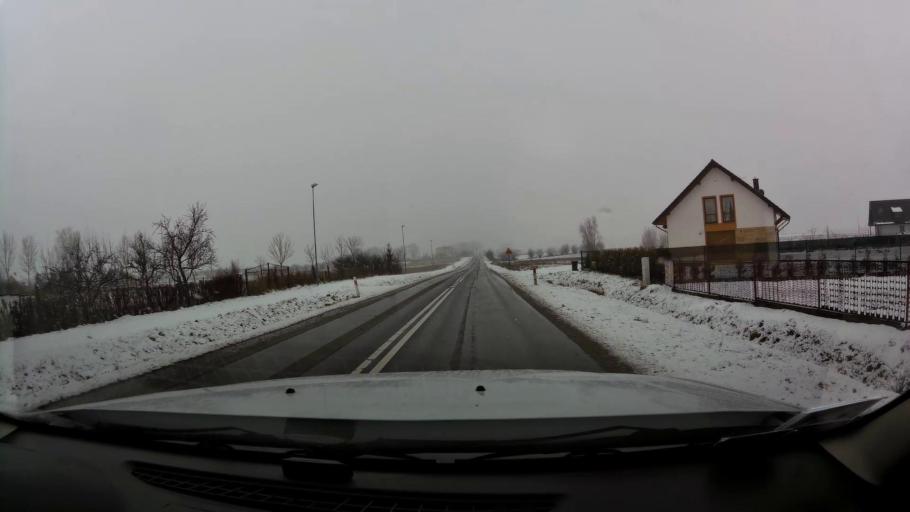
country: PL
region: West Pomeranian Voivodeship
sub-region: Powiat gryficki
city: Trzebiatow
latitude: 54.0931
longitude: 15.2669
